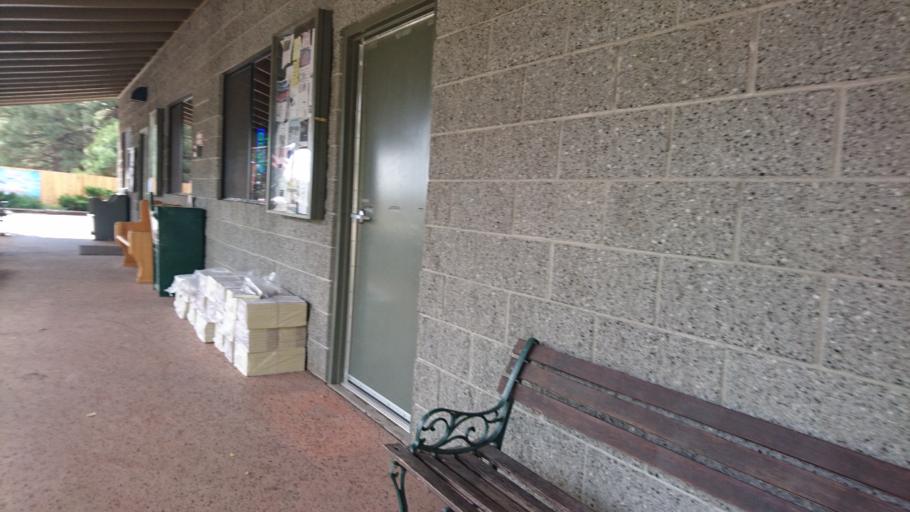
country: US
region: Arizona
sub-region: Coconino County
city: Parks
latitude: 35.2574
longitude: -111.9394
